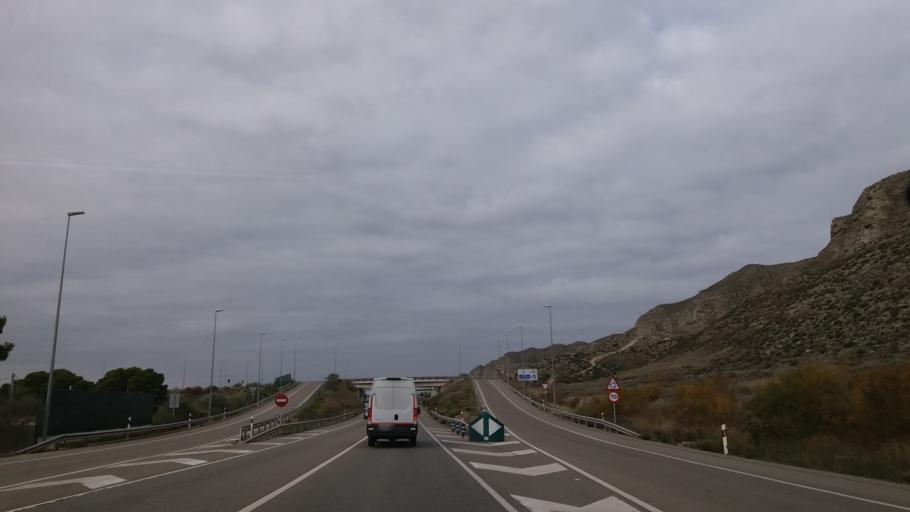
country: ES
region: Aragon
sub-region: Provincia de Zaragoza
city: Villafranca de Ebro
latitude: 41.5815
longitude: -0.6538
